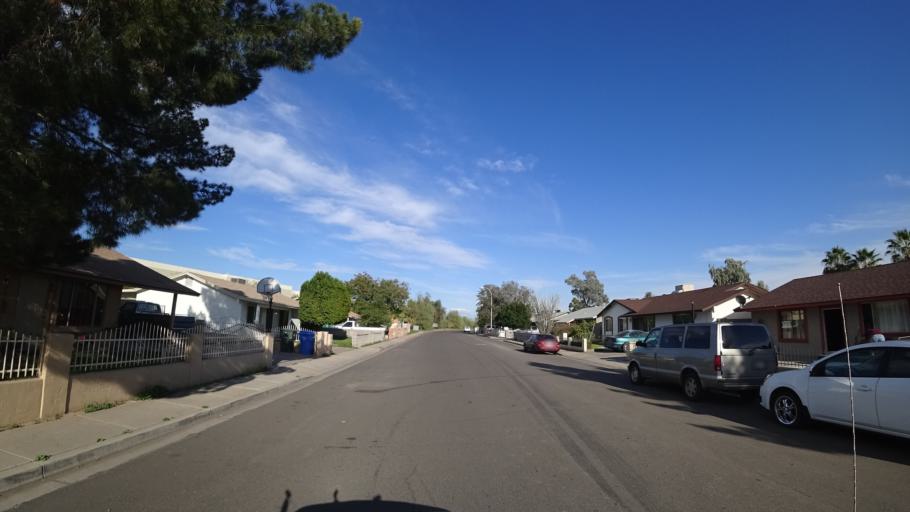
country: US
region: Arizona
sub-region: Maricopa County
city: Tolleson
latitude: 33.4583
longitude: -112.2112
